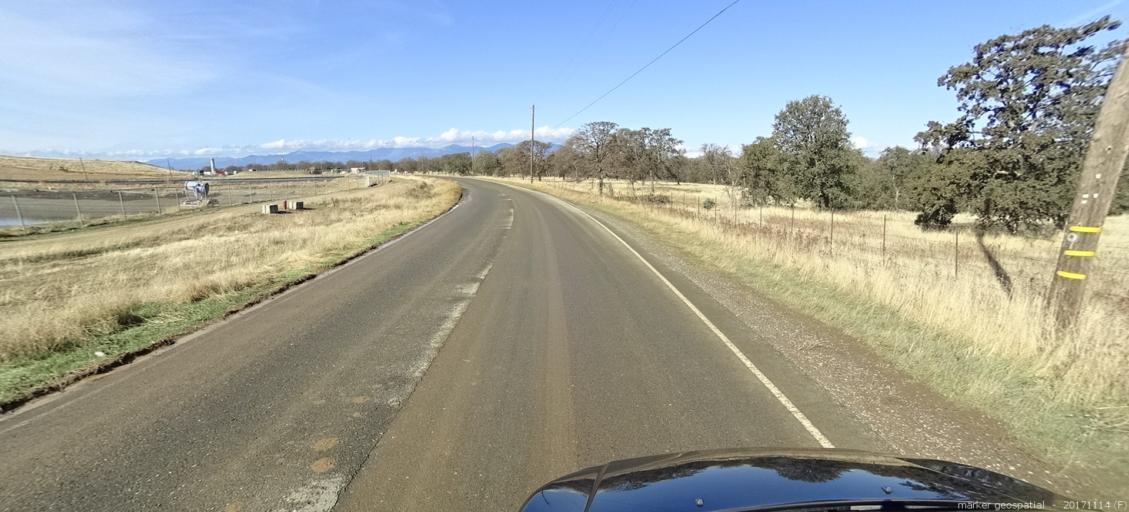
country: US
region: California
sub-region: Shasta County
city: Anderson
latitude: 40.4167
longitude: -122.3513
